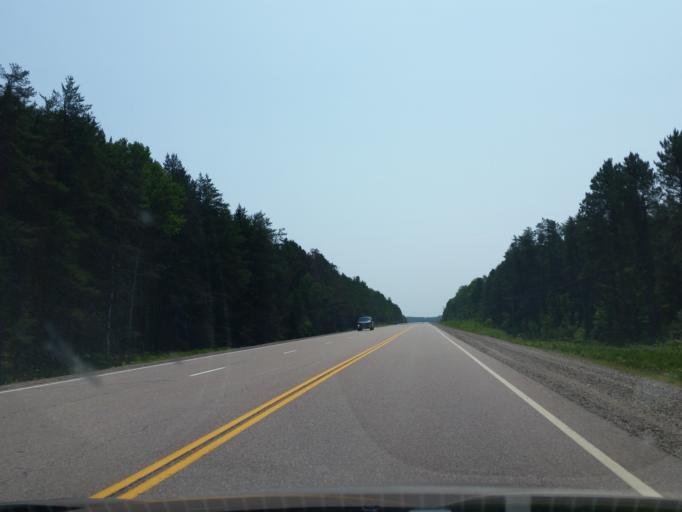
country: CA
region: Ontario
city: Deep River
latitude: 46.1755
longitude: -77.8334
